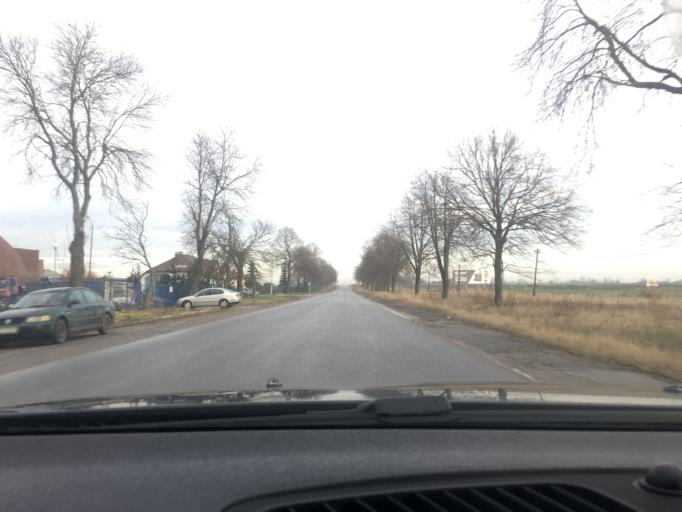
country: PL
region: Swietokrzyskie
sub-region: Powiat jedrzejowski
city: Jedrzejow
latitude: 50.6510
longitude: 20.3193
